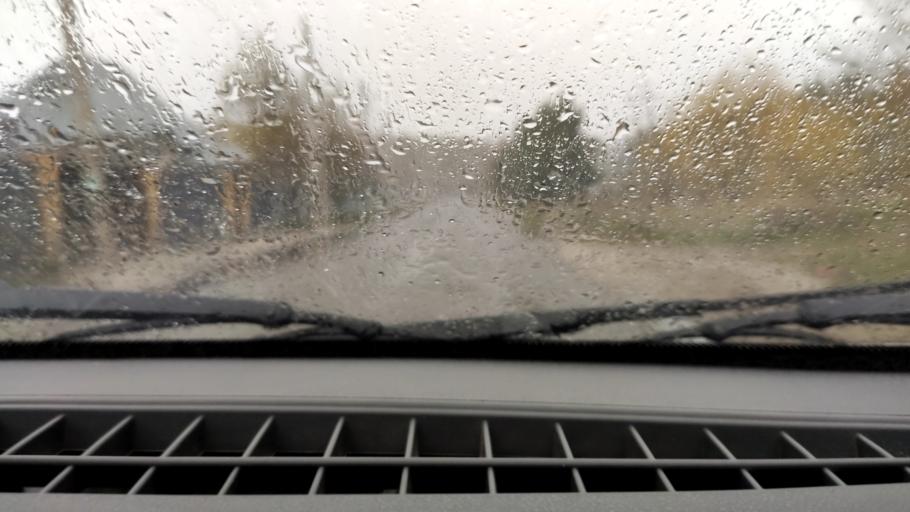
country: RU
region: Voronezj
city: Somovo
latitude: 51.7392
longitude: 39.2963
